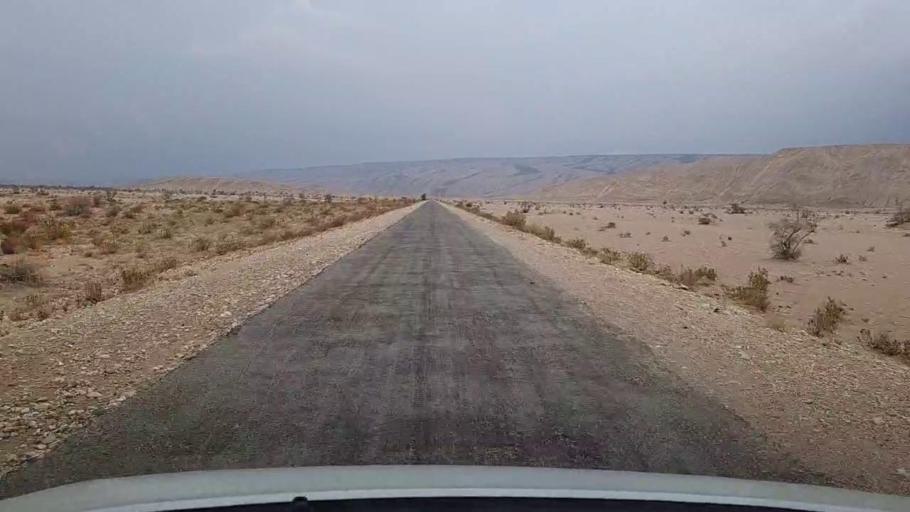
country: PK
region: Sindh
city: Sehwan
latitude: 26.2447
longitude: 67.7154
